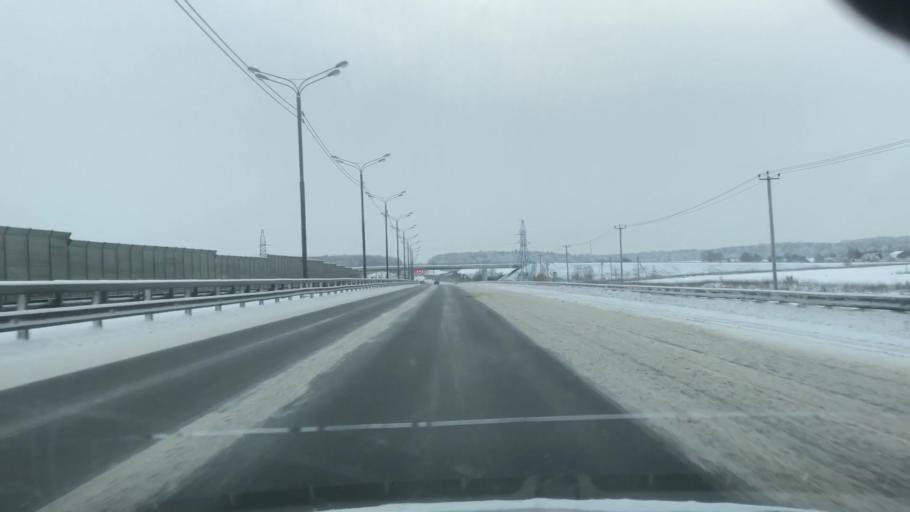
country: RU
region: Moskovskaya
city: Mikhnevo
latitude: 55.1898
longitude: 37.8964
